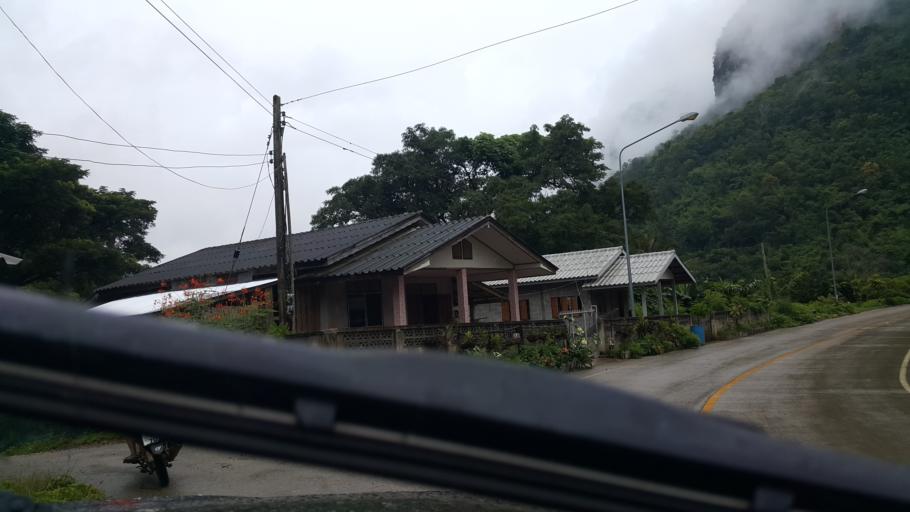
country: TH
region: Phayao
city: Chiang Kham
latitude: 19.5006
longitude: 100.4561
